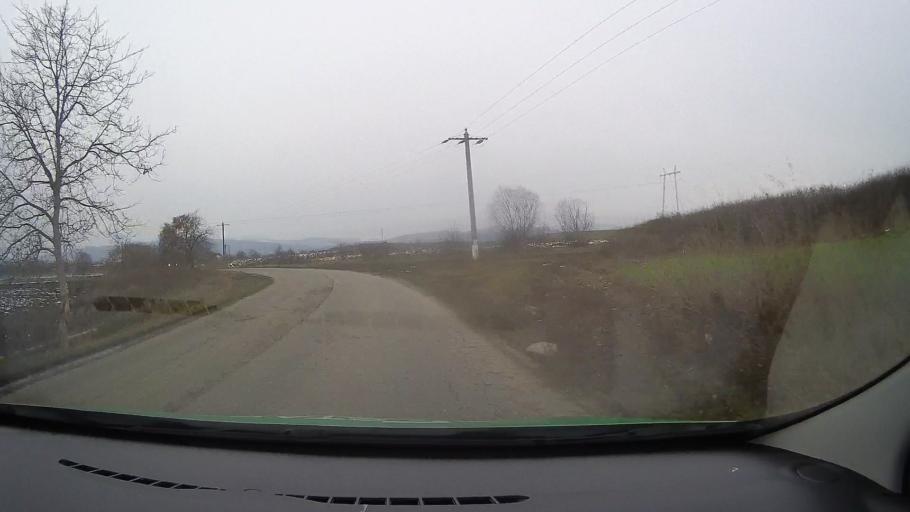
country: RO
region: Hunedoara
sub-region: Comuna Romos
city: Romos
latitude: 45.8746
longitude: 23.2666
